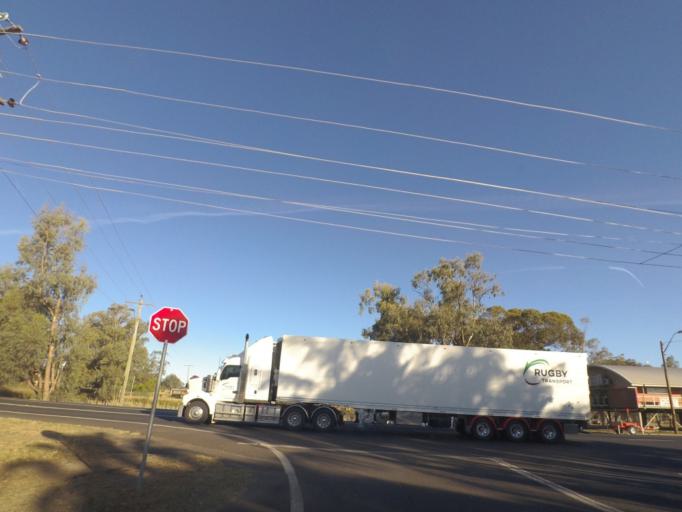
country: AU
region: New South Wales
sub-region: Forbes
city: Forbes
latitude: -33.3840
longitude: 148.0112
